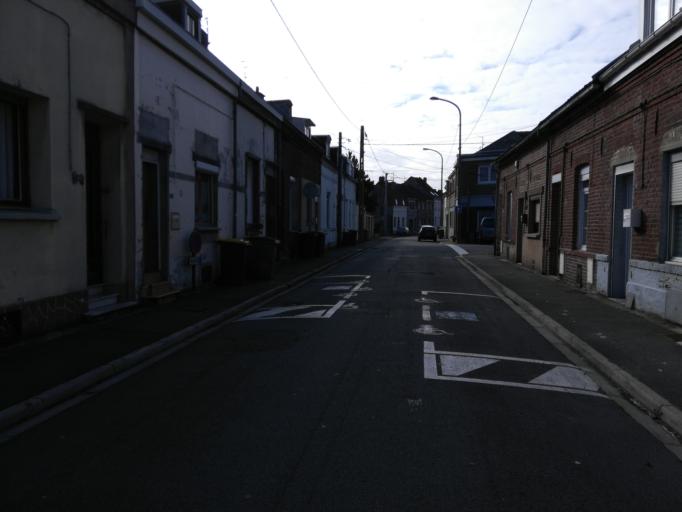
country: FR
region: Nord-Pas-de-Calais
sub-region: Departement du Pas-de-Calais
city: Montigny-en-Gohelle
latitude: 50.4262
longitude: 2.9471
